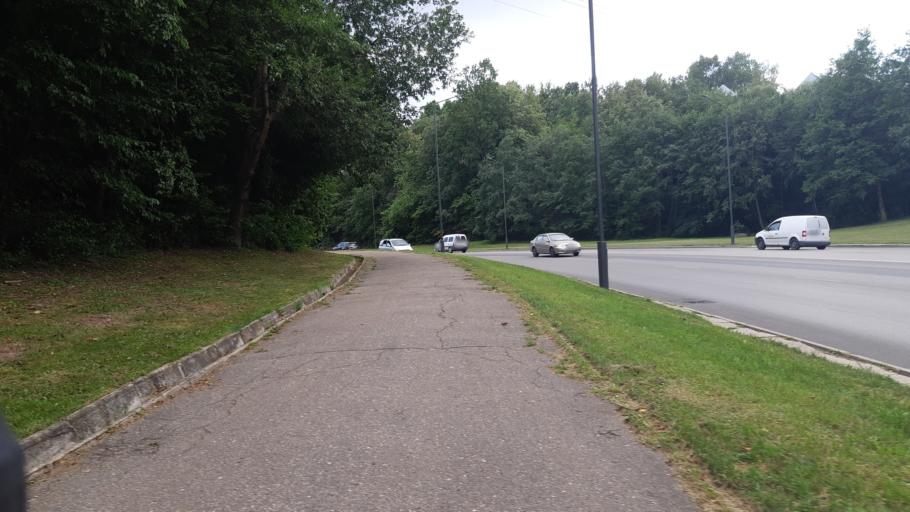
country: LT
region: Kauno apskritis
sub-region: Kaunas
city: Eiguliai
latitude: 54.9284
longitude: 23.9201
